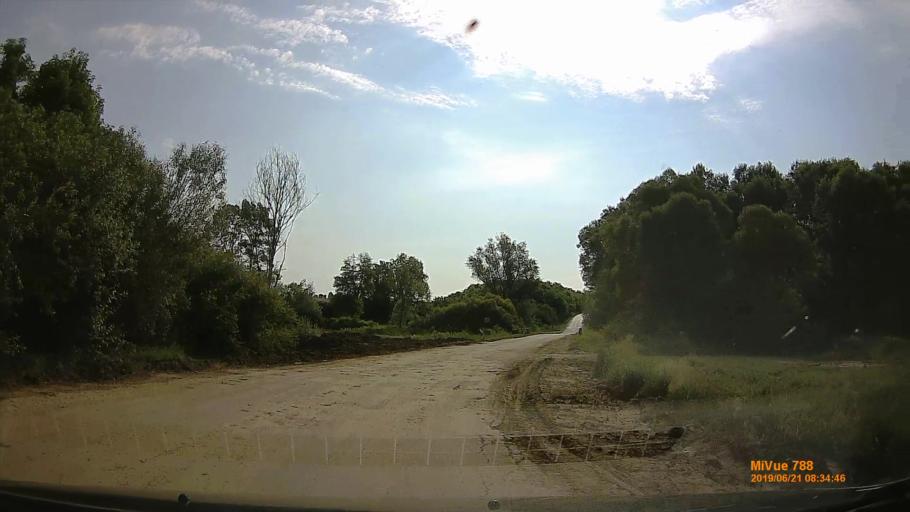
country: HU
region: Baranya
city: Buekkoesd
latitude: 46.1700
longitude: 17.8893
